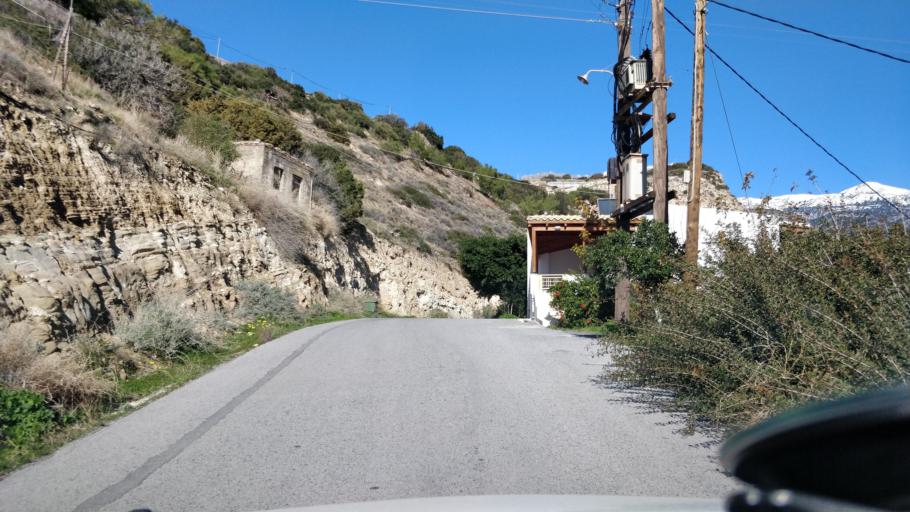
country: GR
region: Crete
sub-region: Nomos Lasithiou
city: Gra Liyia
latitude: 34.9876
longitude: 25.4813
